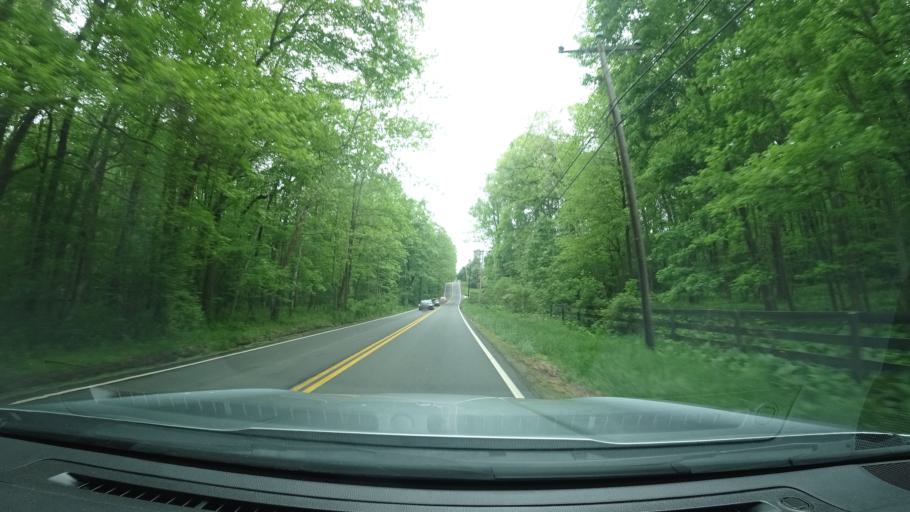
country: US
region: Virginia
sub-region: Fairfax County
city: Oak Hill
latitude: 38.9122
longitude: -77.3634
